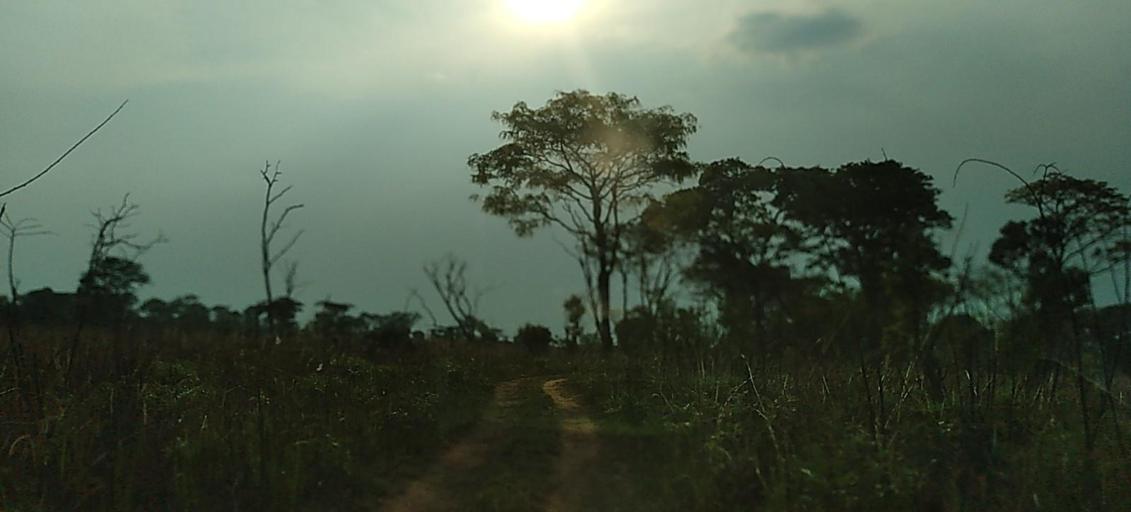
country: ZM
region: North-Western
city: Solwezi
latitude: -12.0451
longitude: 26.0556
